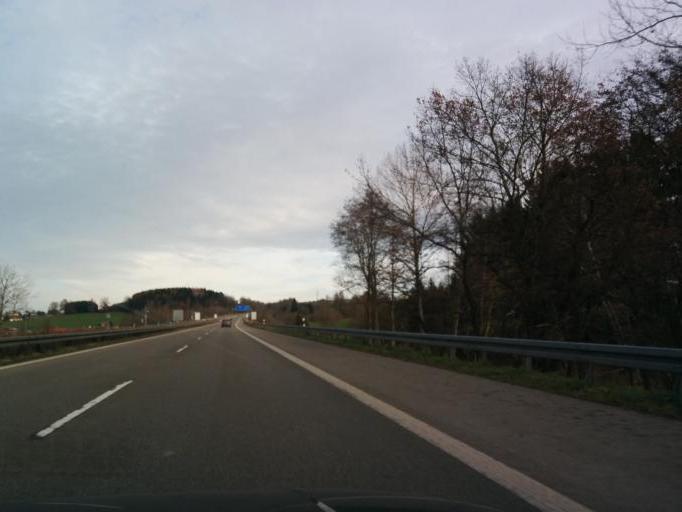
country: DE
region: Bavaria
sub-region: Swabia
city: Durach
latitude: 47.6847
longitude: 10.3378
